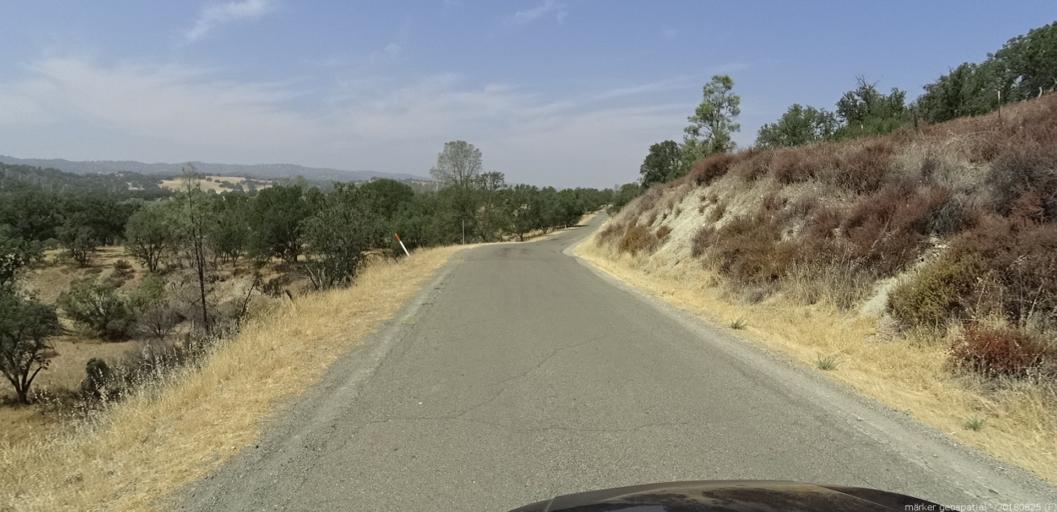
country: US
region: California
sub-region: San Luis Obispo County
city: Shandon
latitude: 35.8722
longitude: -120.4093
